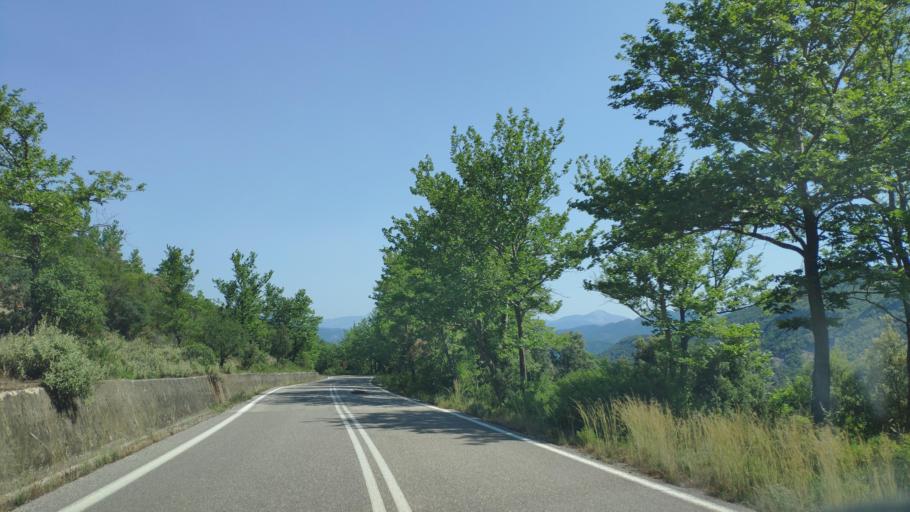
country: GR
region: West Greece
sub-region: Nomos Aitolias kai Akarnanias
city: Lepenou
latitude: 38.7949
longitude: 21.3325
